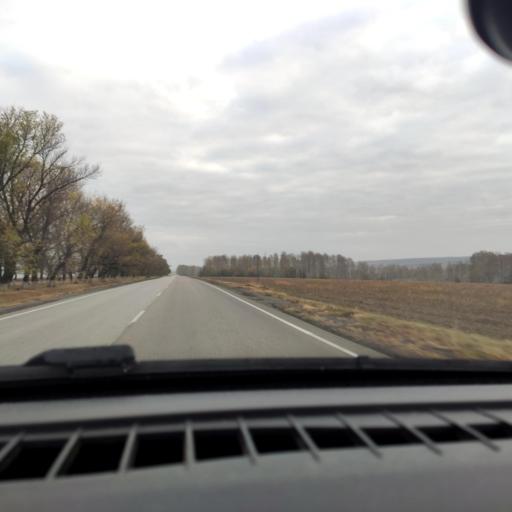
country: RU
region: Belgorod
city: Ilovka
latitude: 50.7572
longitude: 38.7286
